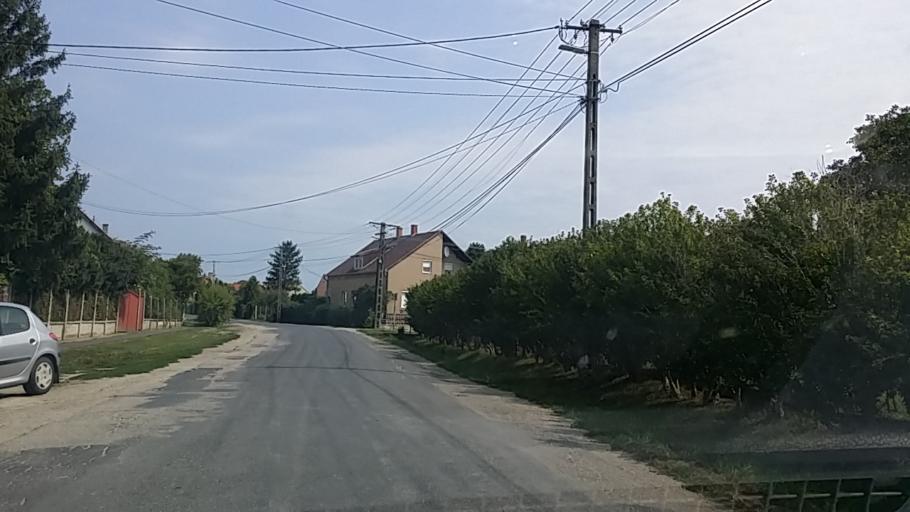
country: HU
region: Gyor-Moson-Sopron
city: Bosarkany
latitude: 47.6885
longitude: 17.2450
